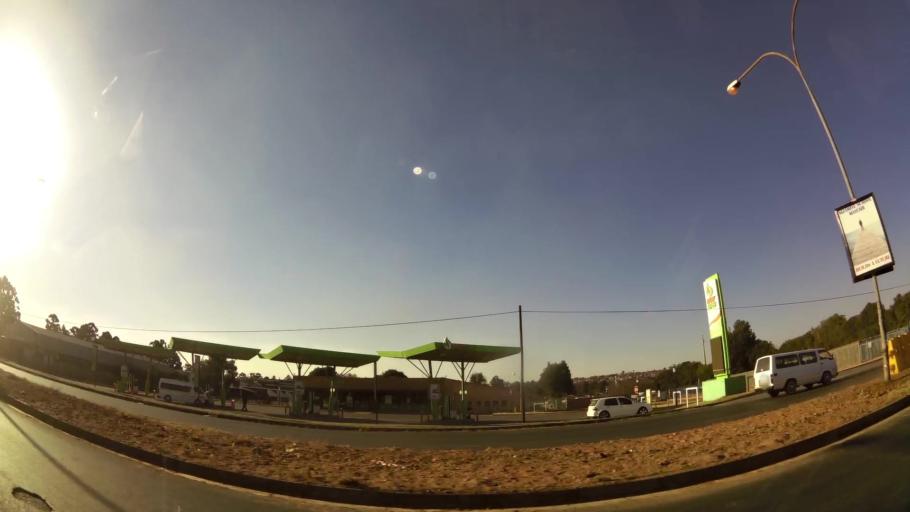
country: ZA
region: Gauteng
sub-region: City of Johannesburg Metropolitan Municipality
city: Johannesburg
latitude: -26.2083
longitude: 27.9833
